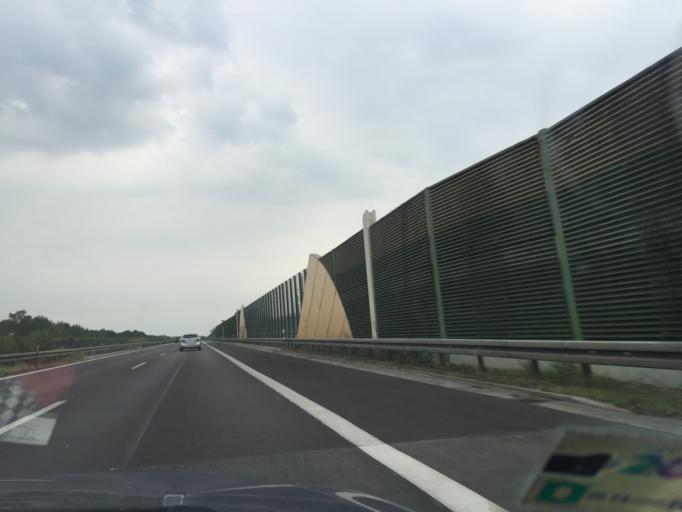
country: DE
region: Brandenburg
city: Bernau bei Berlin
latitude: 52.6739
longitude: 13.5661
